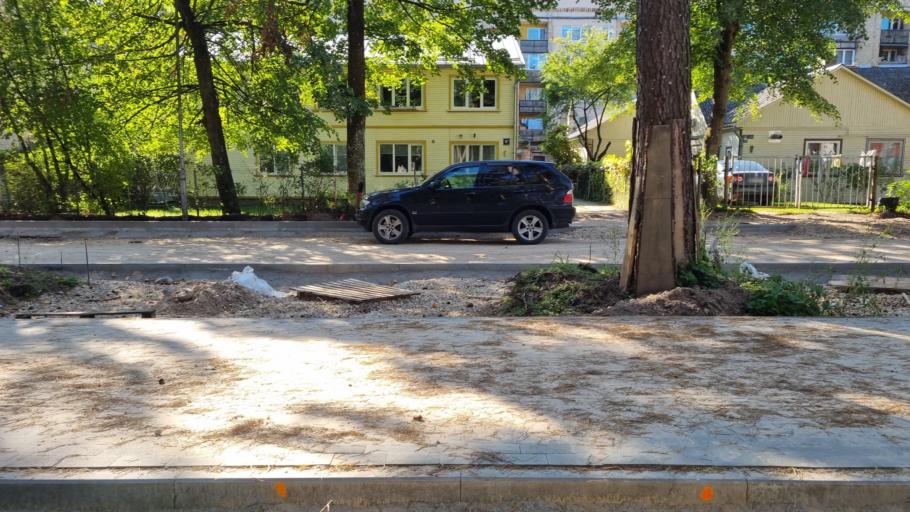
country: LV
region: Babite
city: Pinki
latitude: 56.9804
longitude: 23.8626
